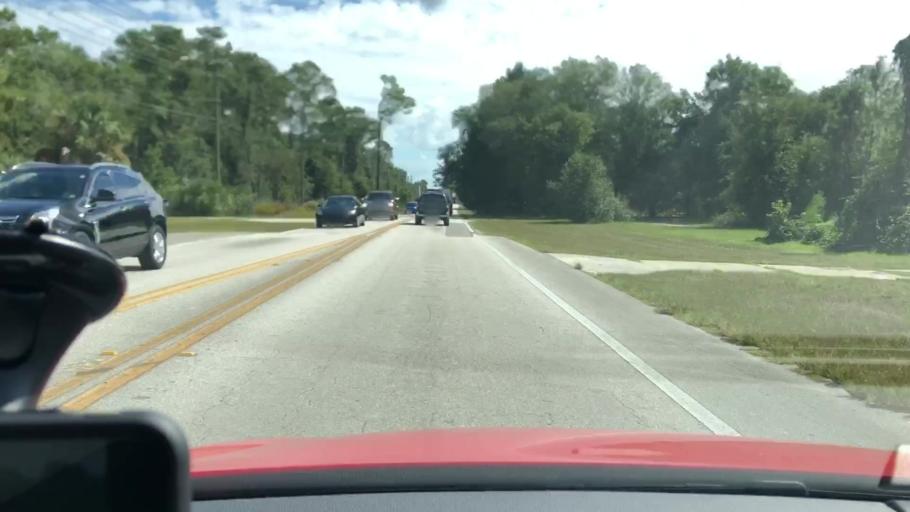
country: US
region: Florida
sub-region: Volusia County
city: Orange City
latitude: 28.9487
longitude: -81.2696
